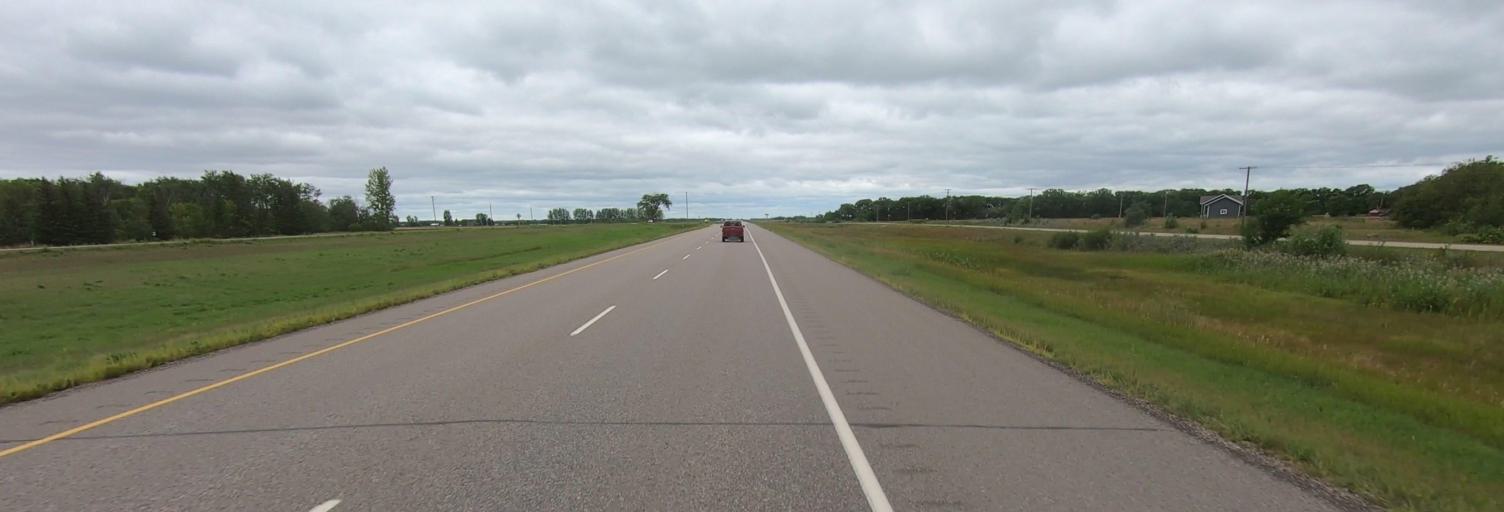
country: CA
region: Manitoba
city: Portage la Prairie
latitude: 49.9755
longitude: -98.6707
